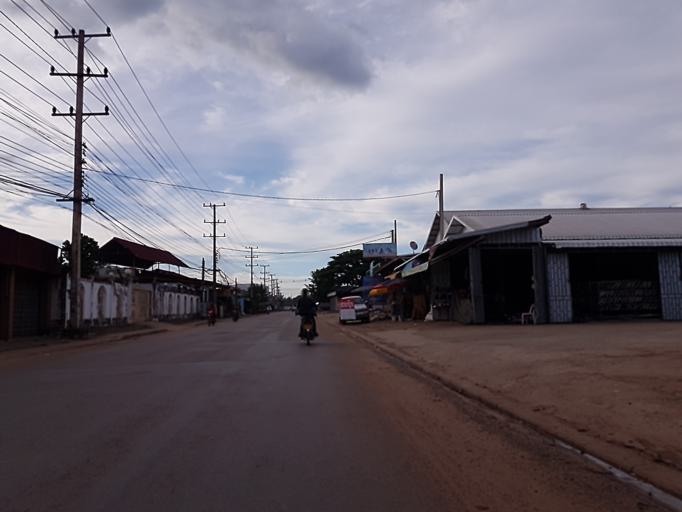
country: LA
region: Vientiane
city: Vientiane
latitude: 17.9857
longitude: 102.5800
